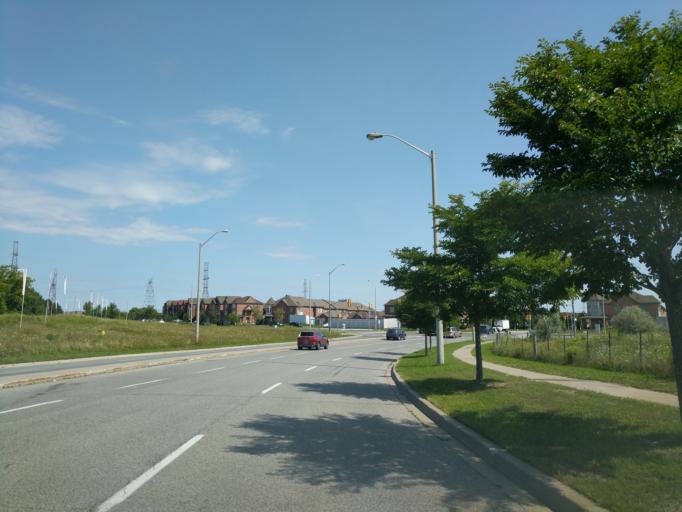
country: CA
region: Ontario
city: Scarborough
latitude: 43.8222
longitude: -79.2306
